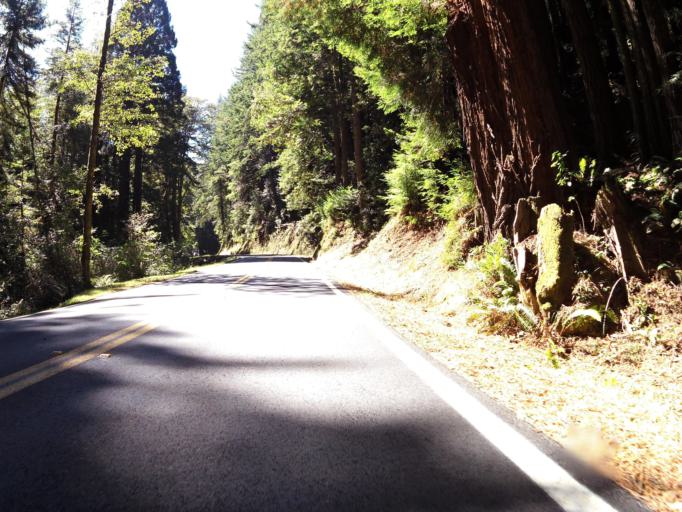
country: US
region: California
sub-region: Humboldt County
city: Redway
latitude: 39.7861
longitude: -123.8189
